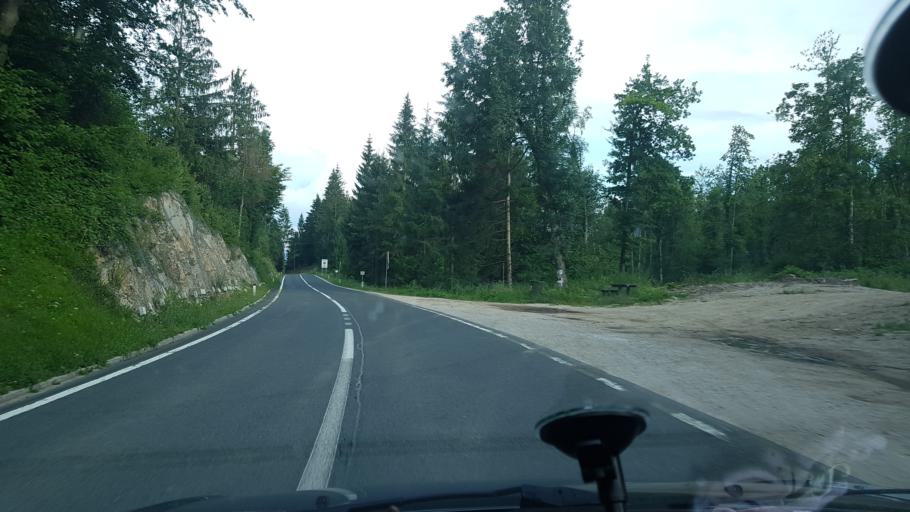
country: SI
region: Ziri
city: Ziri
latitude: 45.9485
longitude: 14.1110
